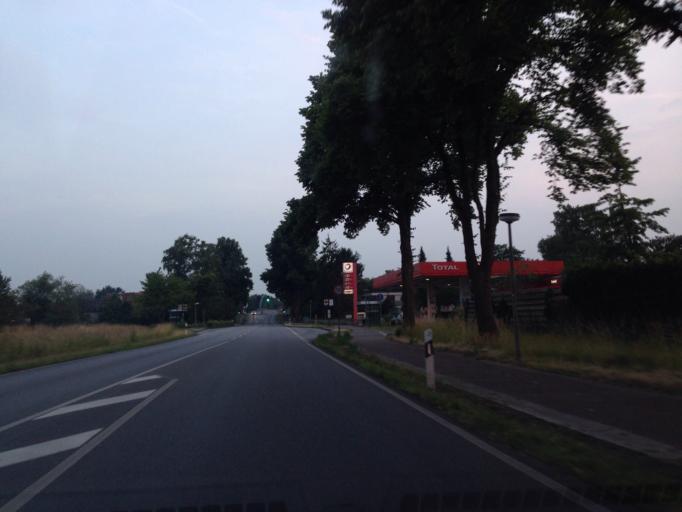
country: DE
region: North Rhine-Westphalia
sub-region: Regierungsbezirk Munster
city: Senden
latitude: 51.8558
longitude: 7.4925
